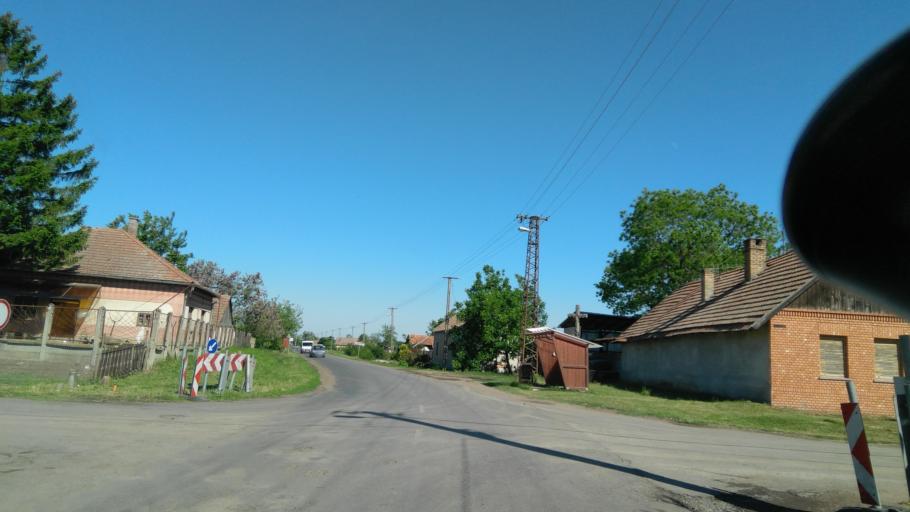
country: HU
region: Bekes
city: Kevermes
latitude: 46.4203
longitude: 21.1762
